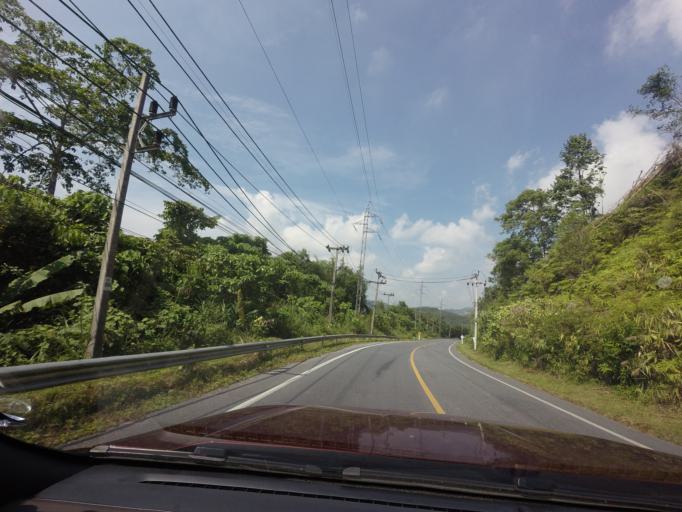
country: TH
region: Yala
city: Betong
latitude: 5.8354
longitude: 101.1195
